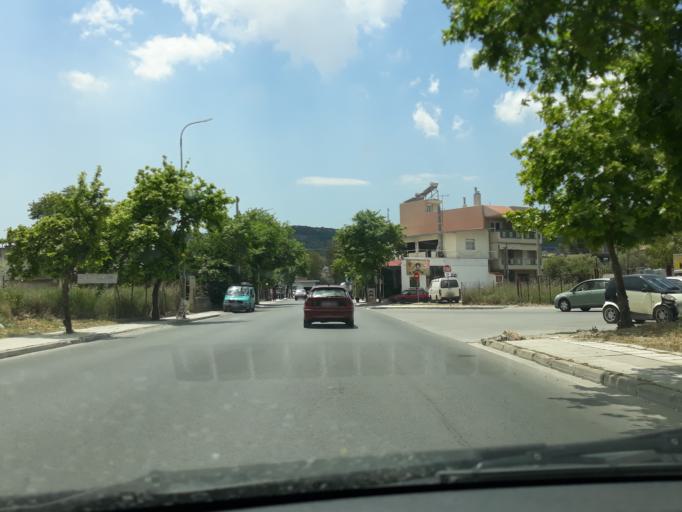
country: GR
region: Attica
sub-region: Nomarchia Dytikis Attikis
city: Ano Liosia
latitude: 38.0759
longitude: 23.7077
